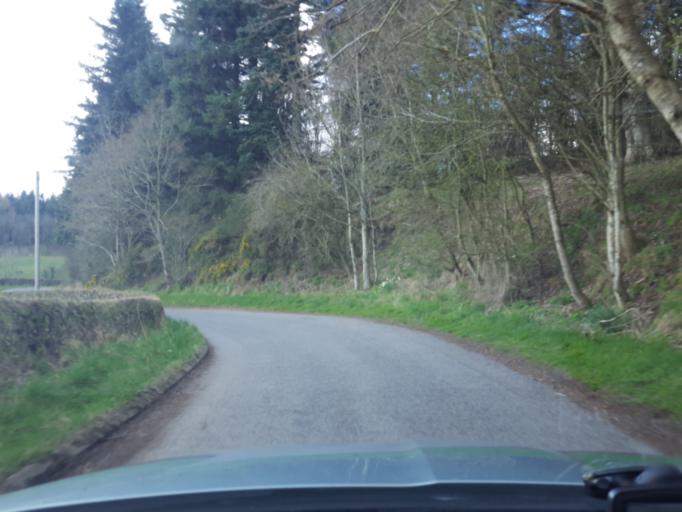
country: GB
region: Scotland
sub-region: Perth and Kinross
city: Scone
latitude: 56.3939
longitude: -3.3851
